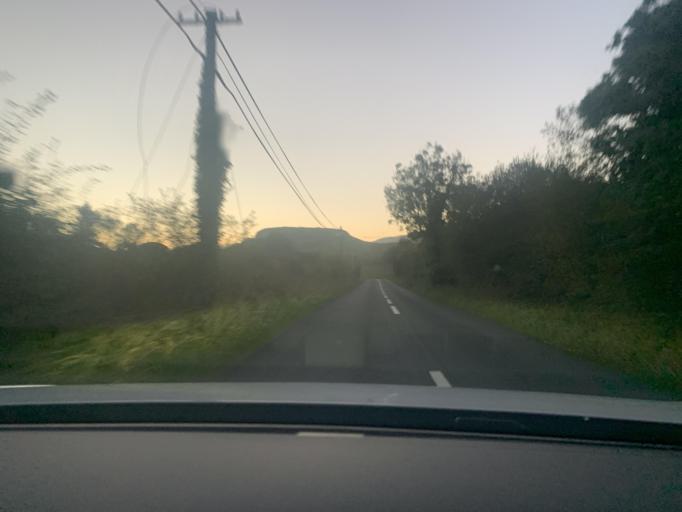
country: IE
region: Connaught
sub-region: County Leitrim
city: Manorhamilton
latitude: 54.2765
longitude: -8.2955
